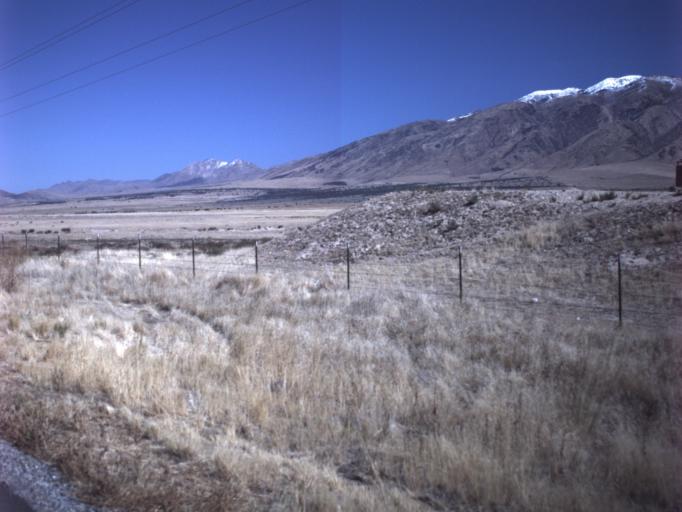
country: US
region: Utah
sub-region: Tooele County
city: Grantsville
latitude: 40.4265
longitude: -112.7488
